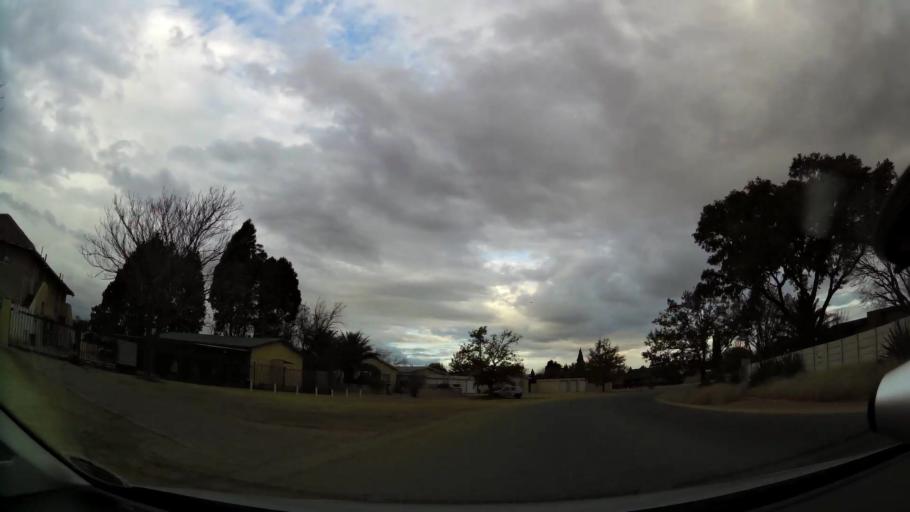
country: ZA
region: Orange Free State
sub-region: Lejweleputswa District Municipality
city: Welkom
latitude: -27.9580
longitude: 26.7242
